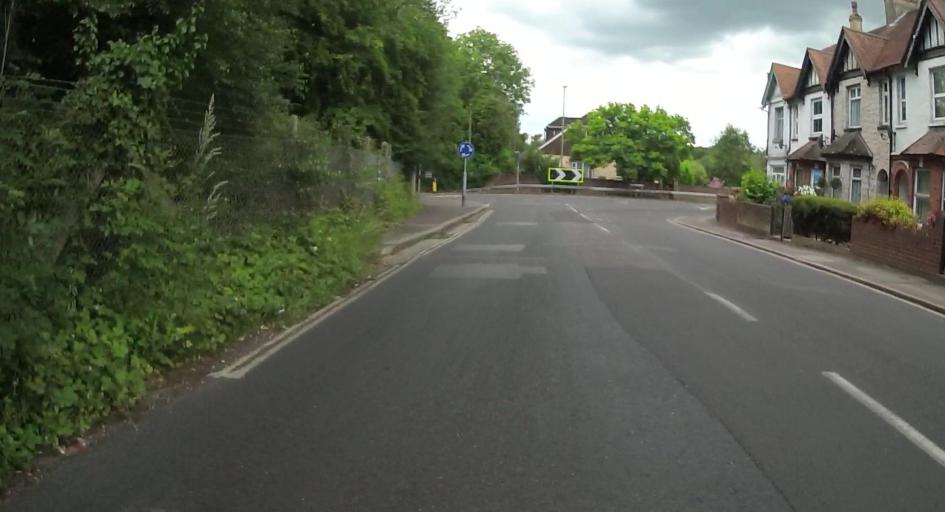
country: GB
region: England
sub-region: Hampshire
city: Aldershot
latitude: 51.2383
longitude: -0.7672
